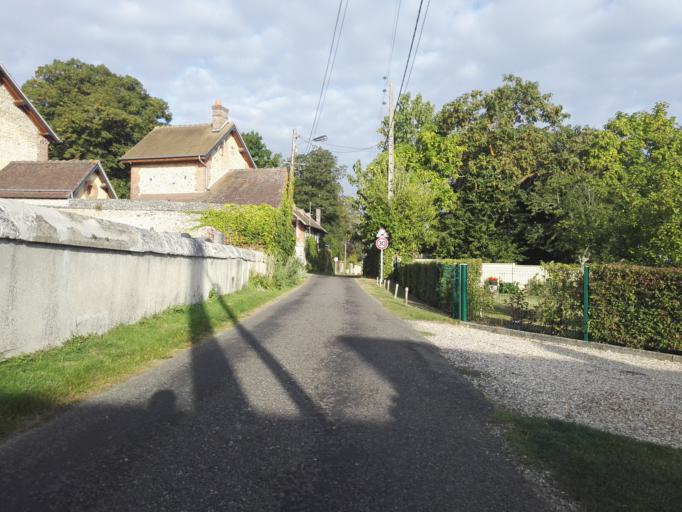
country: FR
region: Haute-Normandie
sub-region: Departement de l'Eure
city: Menilles
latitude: 49.0410
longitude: 1.3151
